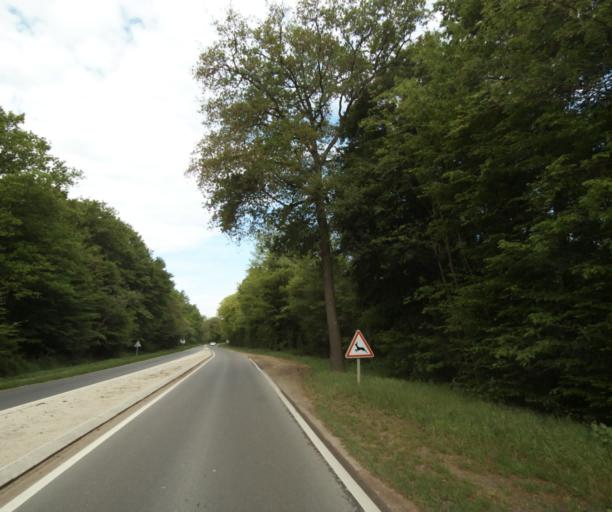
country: FR
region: Ile-de-France
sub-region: Departement des Yvelines
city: Chapet
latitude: 48.9922
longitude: 1.9414
